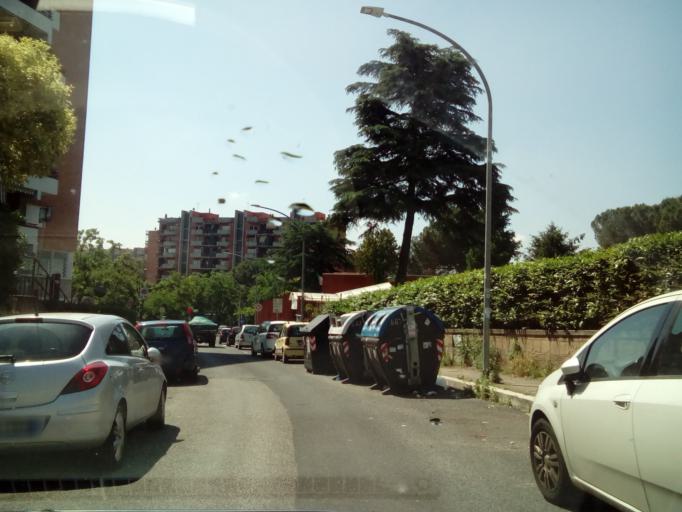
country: IT
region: Latium
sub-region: Citta metropolitana di Roma Capitale
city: Rome
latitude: 41.8890
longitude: 12.5840
